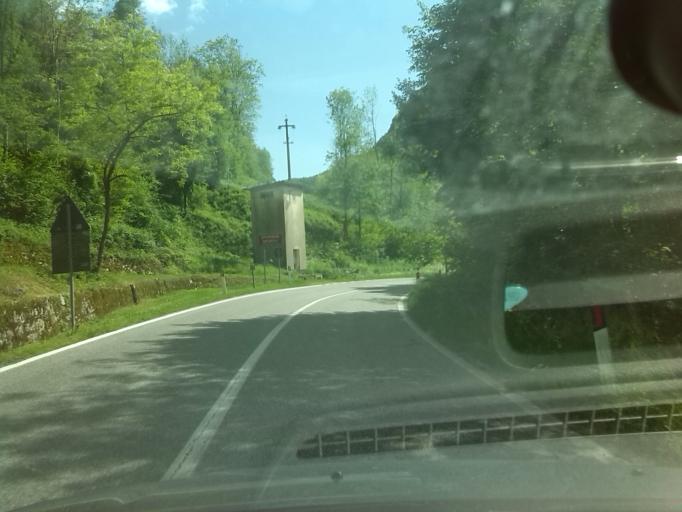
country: IT
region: Friuli Venezia Giulia
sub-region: Provincia di Udine
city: Pulfero
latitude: 46.1993
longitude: 13.4711
